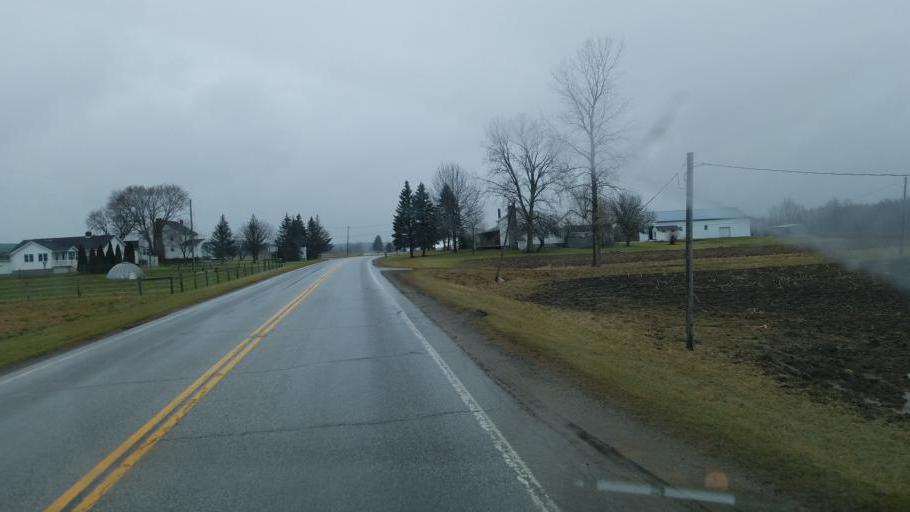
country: US
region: Ohio
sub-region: Geauga County
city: Middlefield
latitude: 41.4255
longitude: -80.9554
